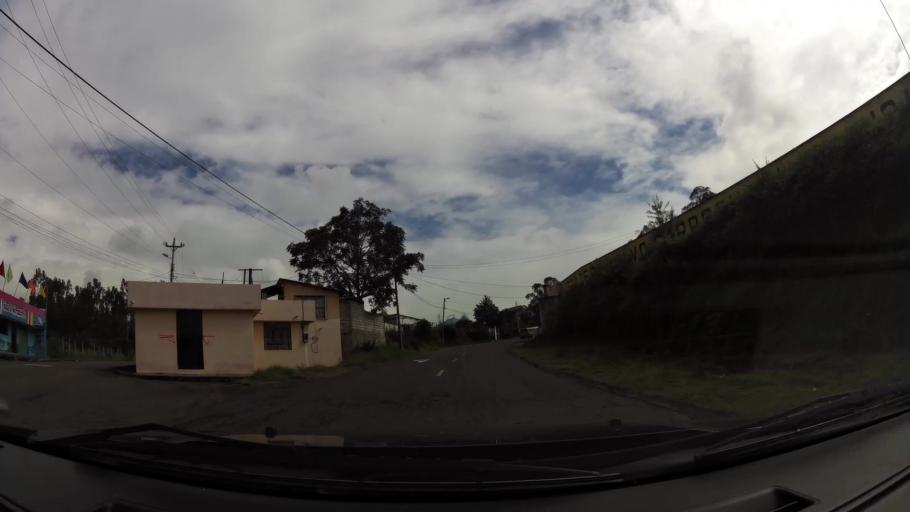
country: EC
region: Pichincha
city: Sangolqui
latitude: -0.3035
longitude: -78.4145
